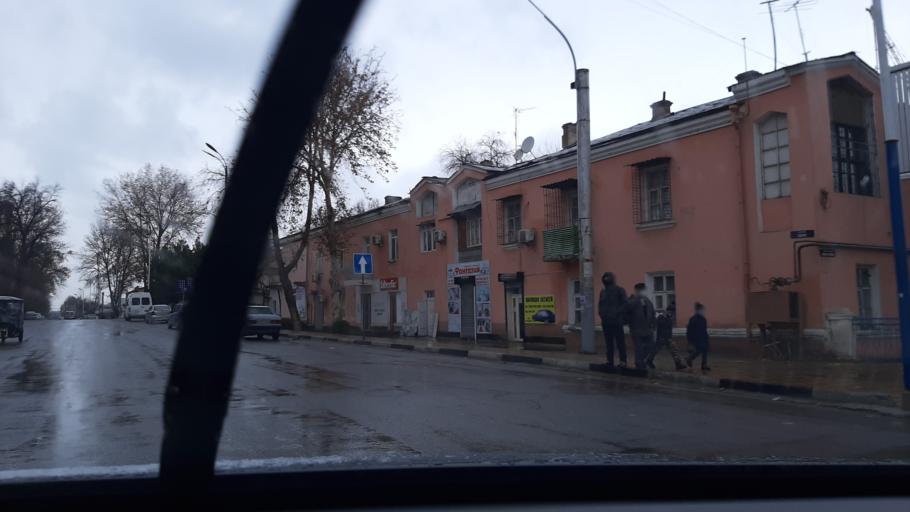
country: TJ
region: Viloyati Sughd
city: Khujand
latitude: 40.2781
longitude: 69.6406
